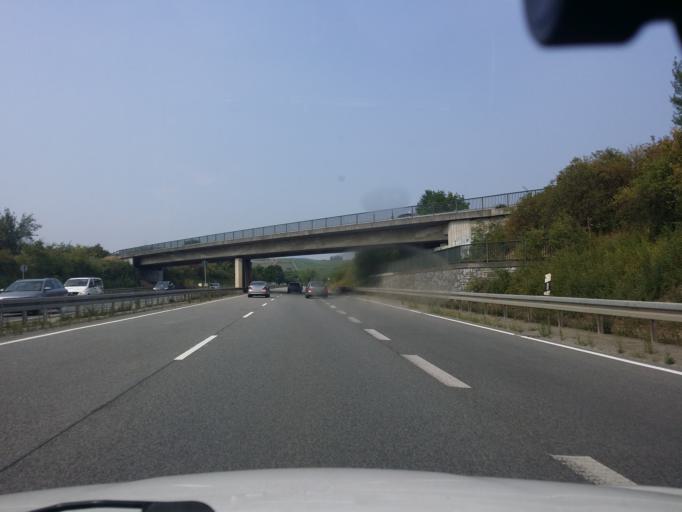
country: DE
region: Hesse
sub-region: Regierungsbezirk Darmstadt
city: Eltville
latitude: 50.0294
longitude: 8.1069
